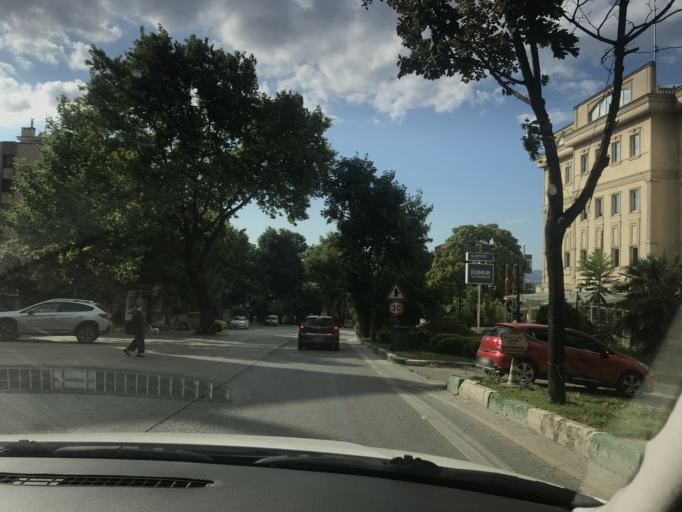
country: TR
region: Bursa
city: Yildirim
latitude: 40.2046
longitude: 29.0203
